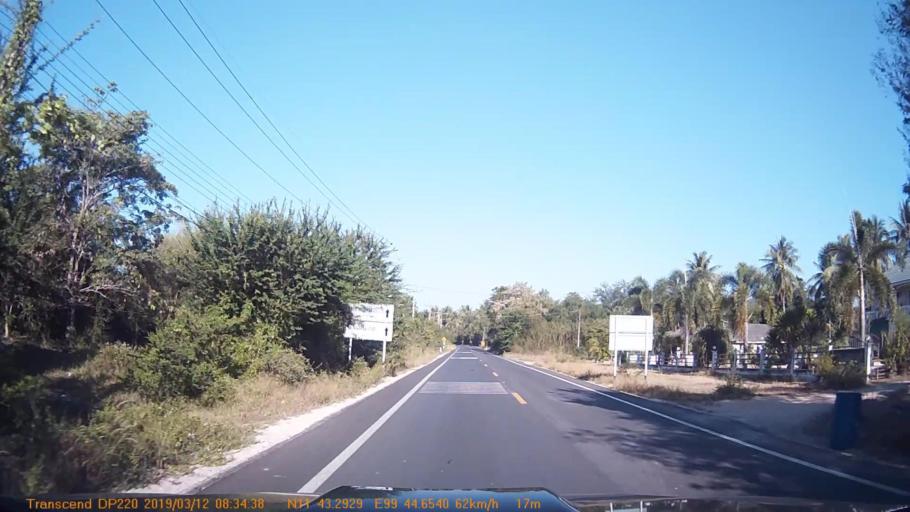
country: TH
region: Prachuap Khiri Khan
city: Prachuap Khiri Khan
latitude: 11.7217
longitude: 99.7439
